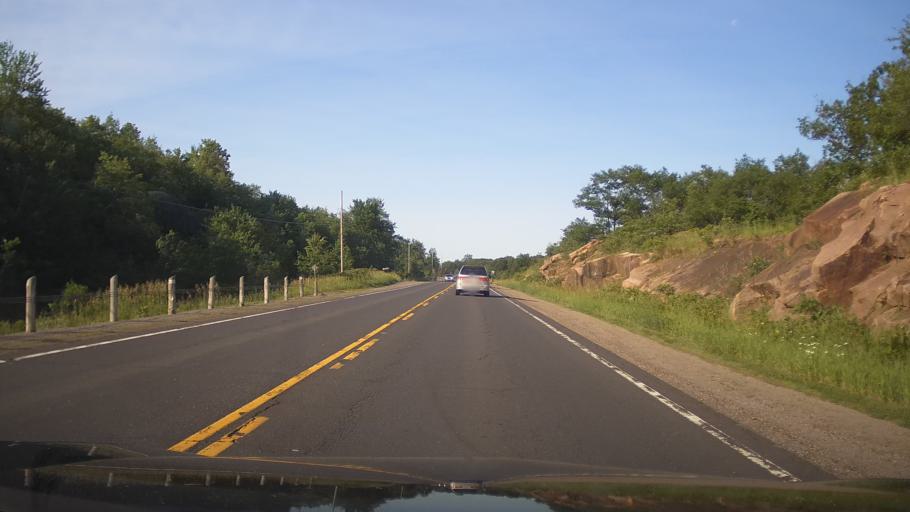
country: CA
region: Ontario
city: Greater Napanee
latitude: 44.6077
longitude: -77.1828
